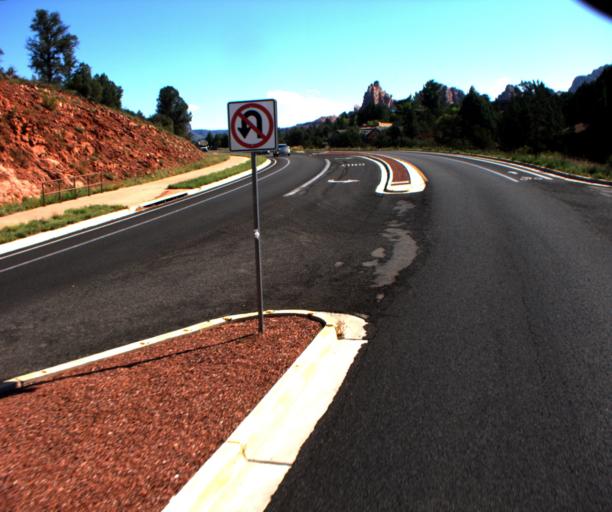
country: US
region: Arizona
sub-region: Coconino County
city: Sedona
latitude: 34.8449
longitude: -111.7676
